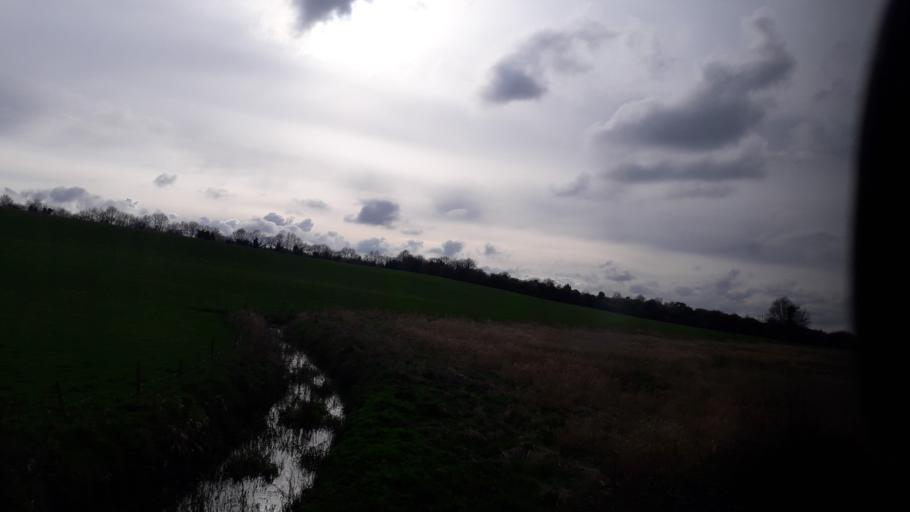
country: IE
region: Leinster
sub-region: Kildare
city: Kilcock
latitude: 53.4166
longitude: -6.7009
